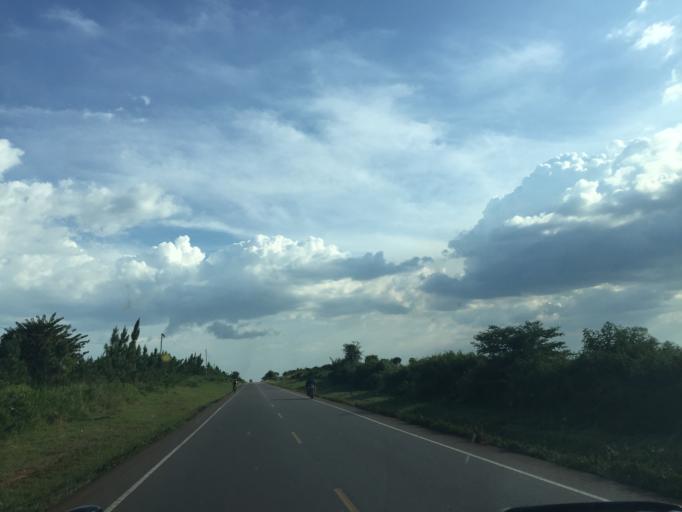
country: UG
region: Central Region
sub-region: Nakasongola District
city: Nakasongola
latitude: 1.1277
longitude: 32.4653
